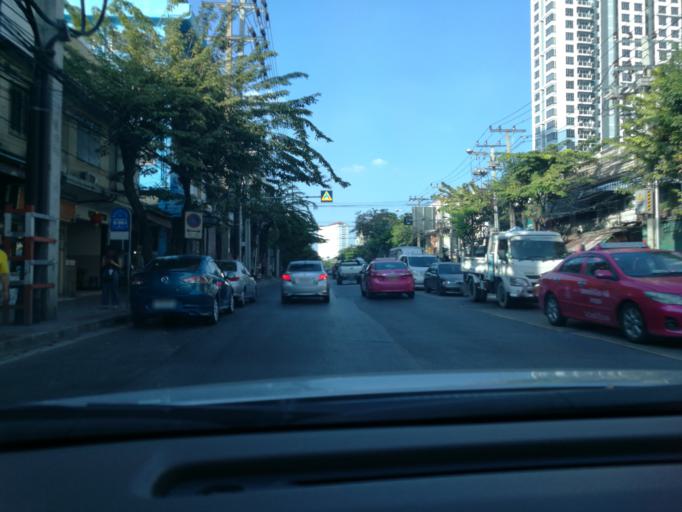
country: TH
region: Bangkok
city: Bang Sue
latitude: 13.8069
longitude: 100.5217
